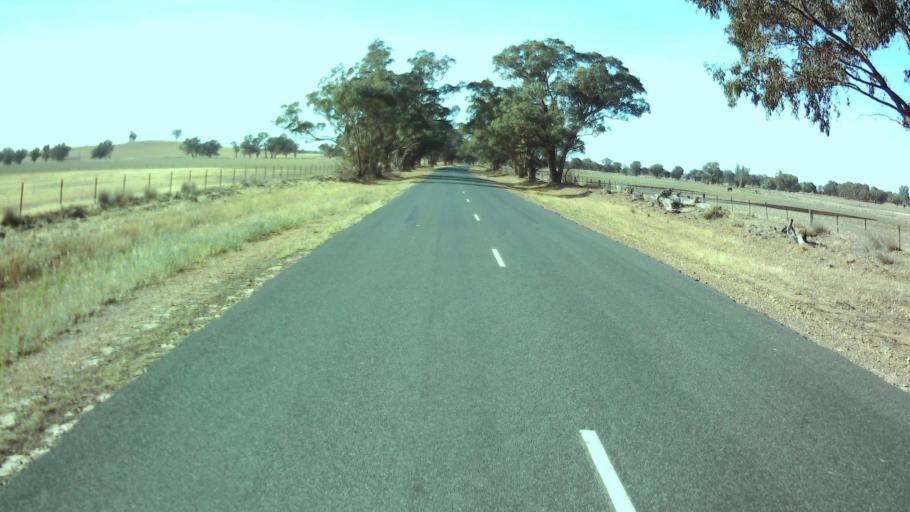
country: AU
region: New South Wales
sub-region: Weddin
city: Grenfell
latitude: -33.9555
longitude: 148.1392
